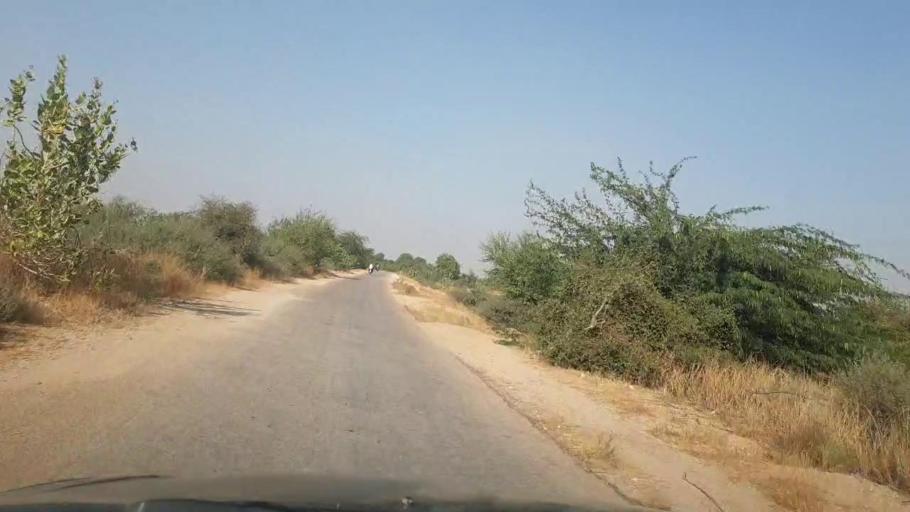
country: PK
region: Sindh
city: Jamshoro
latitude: 25.5271
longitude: 67.8216
